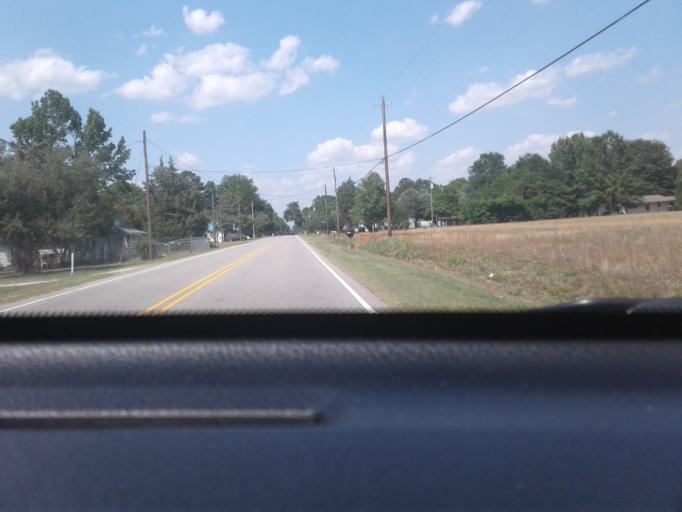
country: US
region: North Carolina
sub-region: Cumberland County
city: Eastover
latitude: 35.1634
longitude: -78.7276
